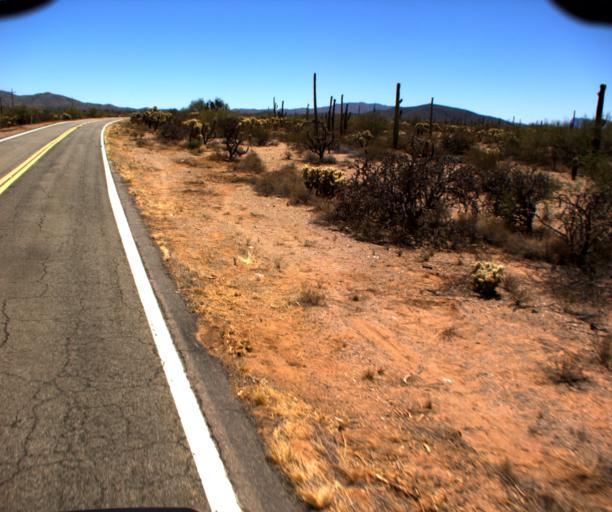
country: US
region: Arizona
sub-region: Pima County
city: Sells
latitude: 32.1830
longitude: -112.3047
